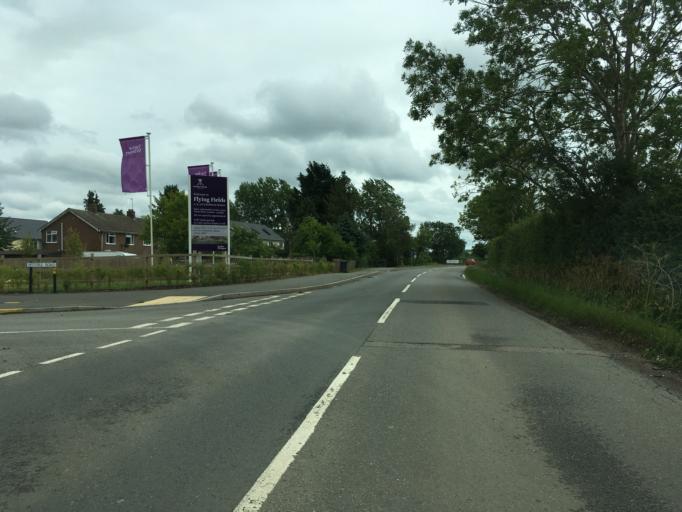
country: GB
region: England
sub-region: Warwickshire
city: Southam
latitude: 52.2480
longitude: -1.3774
